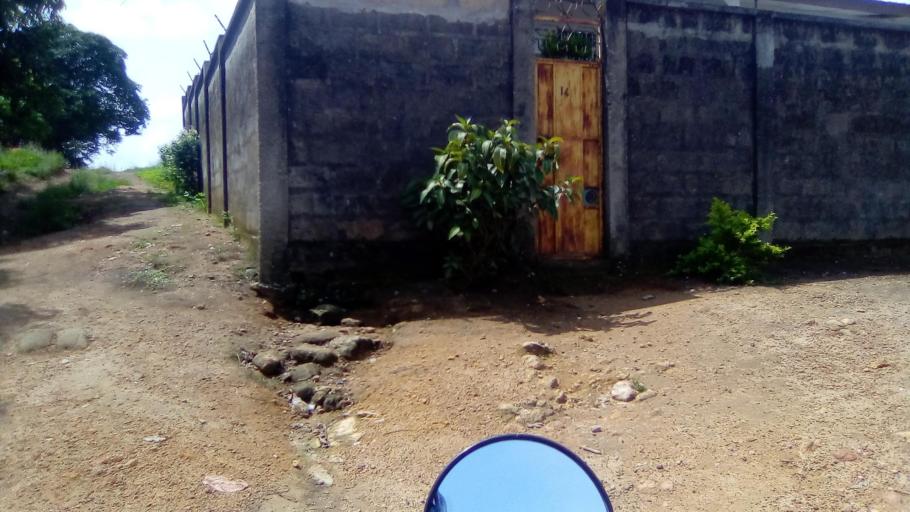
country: SL
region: Southern Province
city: Bo
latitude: 7.9787
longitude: -11.7457
